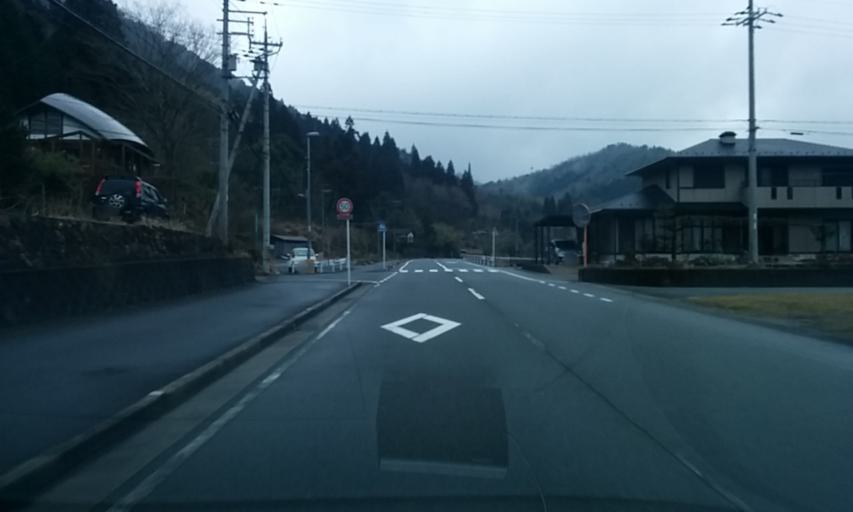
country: JP
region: Kyoto
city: Ayabe
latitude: 35.2453
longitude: 135.2658
